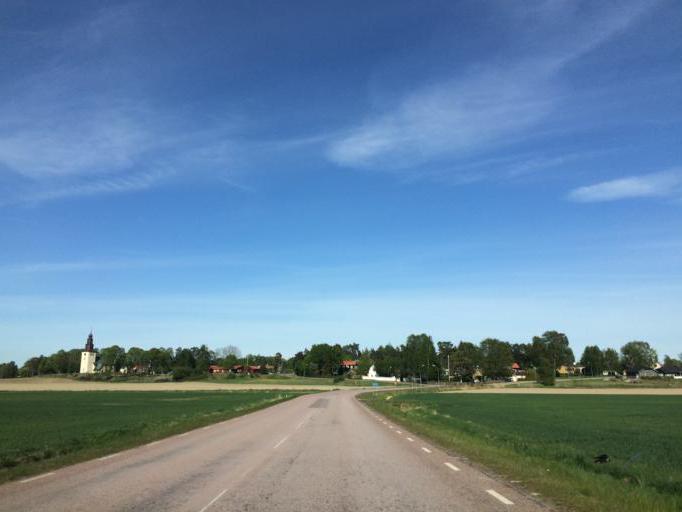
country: SE
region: Soedermanland
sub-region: Eskilstuna Kommun
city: Kvicksund
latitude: 59.4222
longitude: 16.3333
